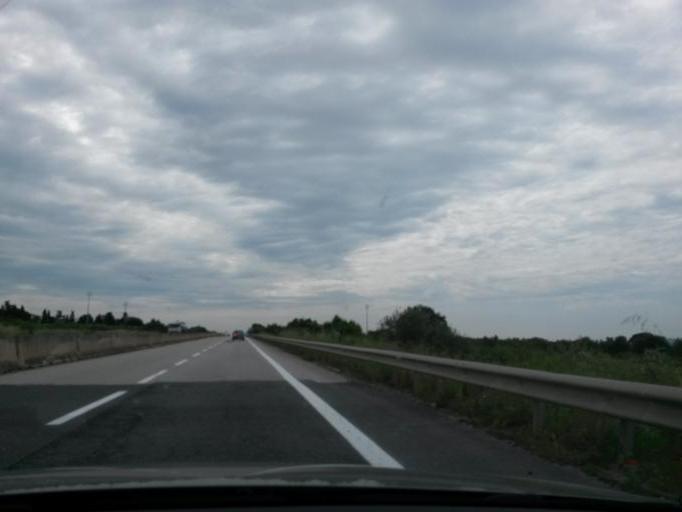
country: IT
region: Tuscany
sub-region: Provincia di Livorno
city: San Vincenzo
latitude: 43.0592
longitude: 10.5636
